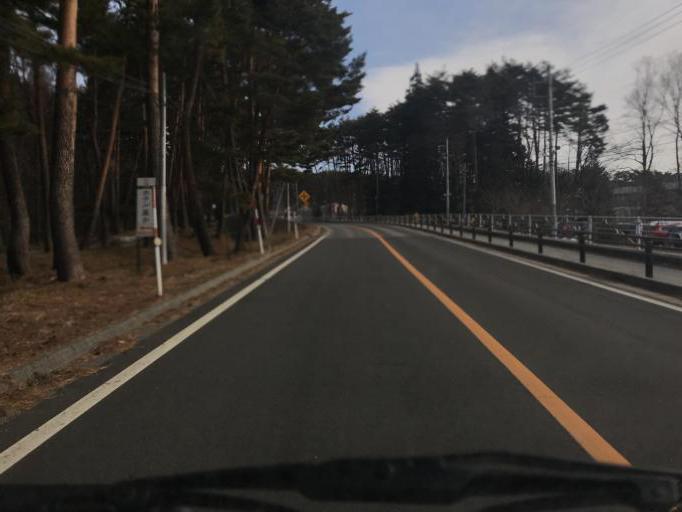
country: JP
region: Nagano
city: Chino
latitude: 35.8775
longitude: 138.3134
